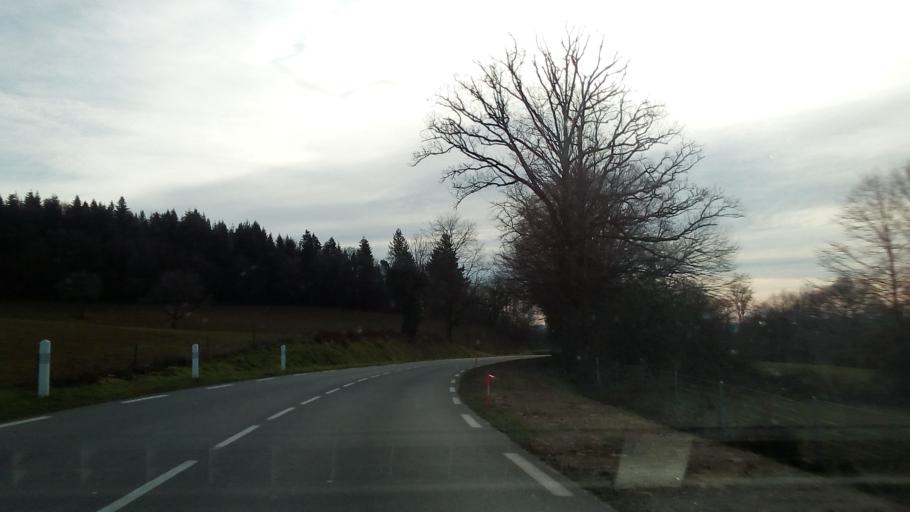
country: FR
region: Limousin
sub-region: Departement de la Correze
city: Naves
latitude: 45.3334
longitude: 1.7608
